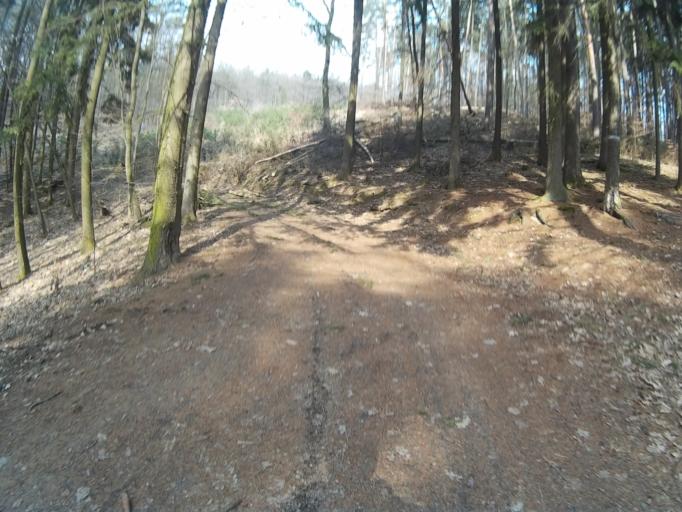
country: CZ
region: South Moravian
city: Pozorice
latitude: 49.2286
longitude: 16.7959
